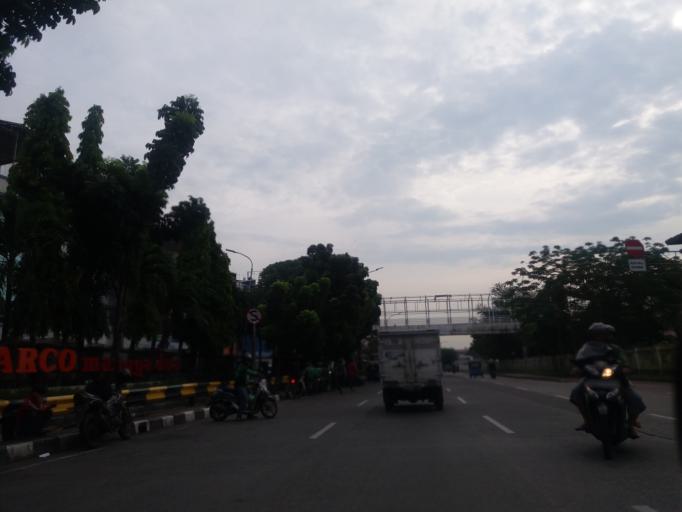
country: ID
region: Jakarta Raya
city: Jakarta
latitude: -6.1355
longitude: 106.8303
